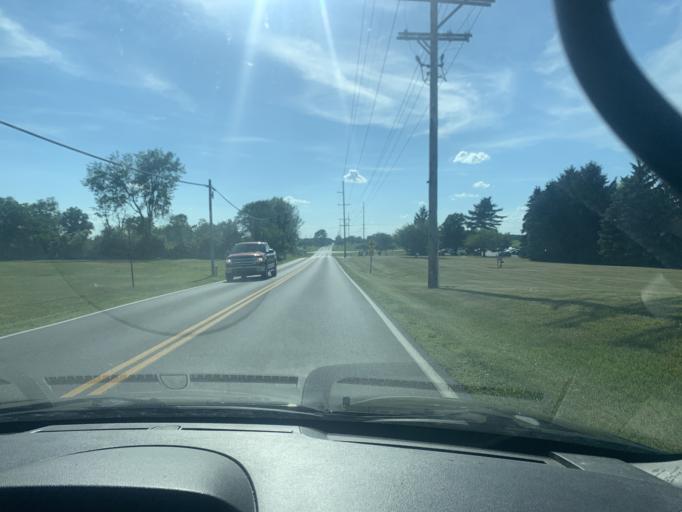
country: US
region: Ohio
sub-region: Logan County
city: Bellefontaine
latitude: 40.3473
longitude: -83.7720
